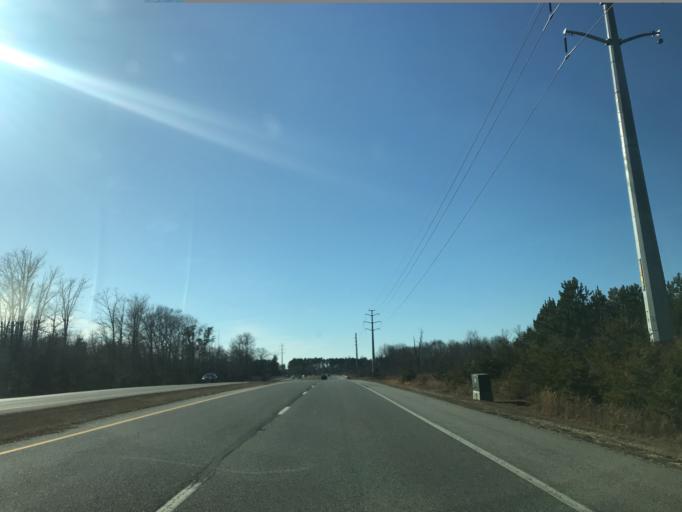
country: US
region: Maryland
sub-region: Charles County
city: La Plata
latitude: 38.5596
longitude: -76.9674
